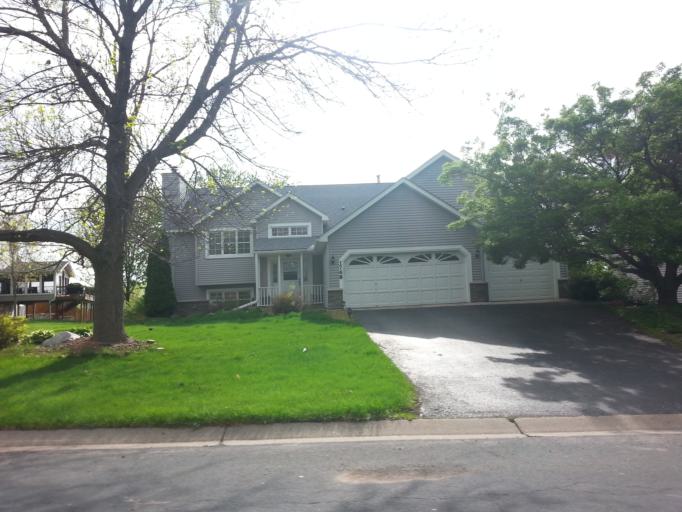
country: US
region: Minnesota
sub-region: Washington County
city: Woodbury
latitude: 44.9230
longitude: -92.9178
